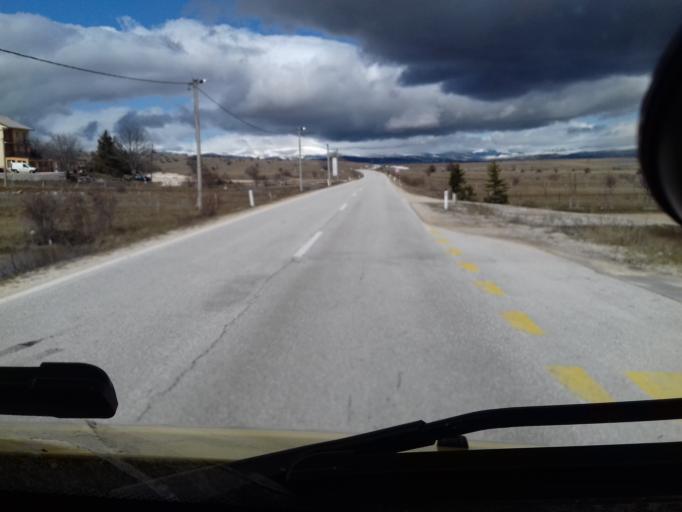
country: BA
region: Federation of Bosnia and Herzegovina
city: Dreznica
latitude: 43.6107
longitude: 17.2684
